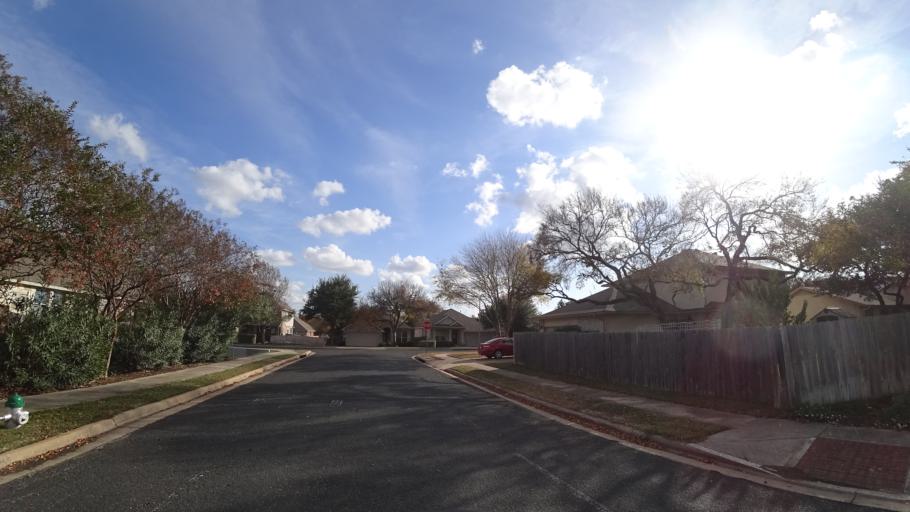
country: US
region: Texas
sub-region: Williamson County
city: Brushy Creek
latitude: 30.5107
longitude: -97.7224
